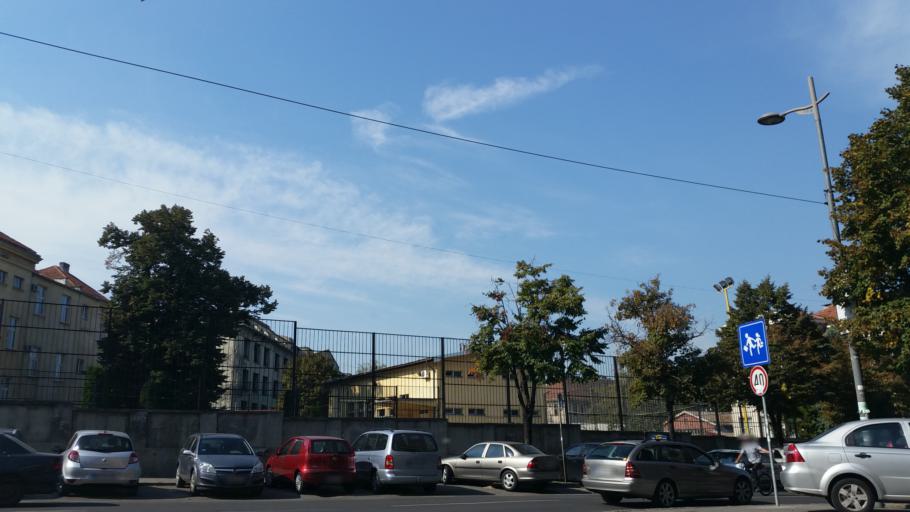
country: RS
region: Central Serbia
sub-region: Belgrade
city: Stari Grad
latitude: 44.8263
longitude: 20.4561
